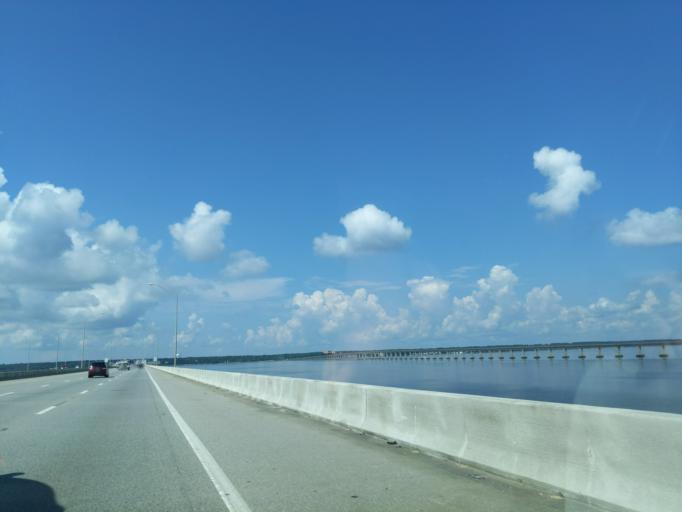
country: US
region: Florida
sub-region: Santa Rosa County
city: Pace
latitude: 30.5258
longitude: -87.1356
